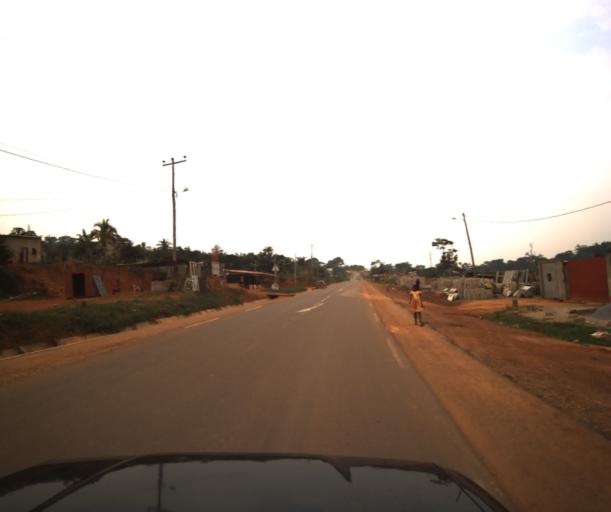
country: CM
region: Centre
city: Mbankomo
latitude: 3.8027
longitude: 11.4535
